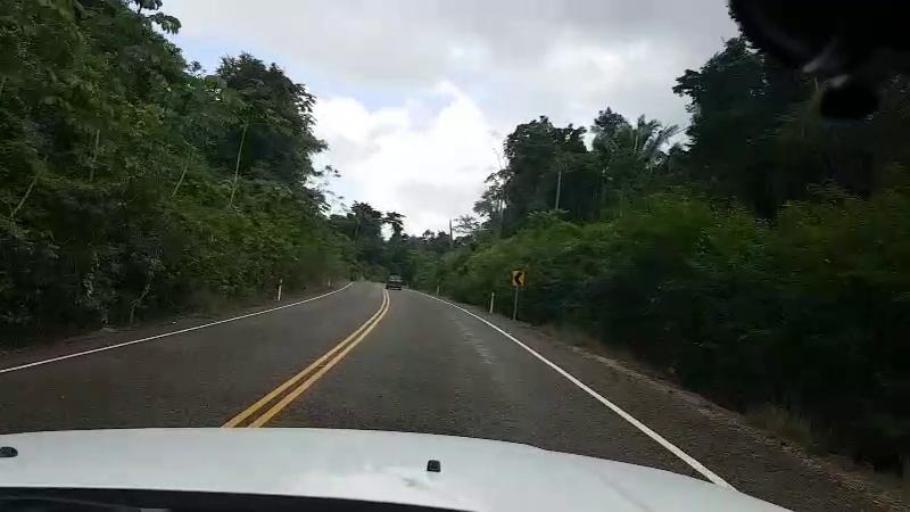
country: BZ
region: Cayo
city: Belmopan
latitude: 17.1541
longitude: -88.6766
